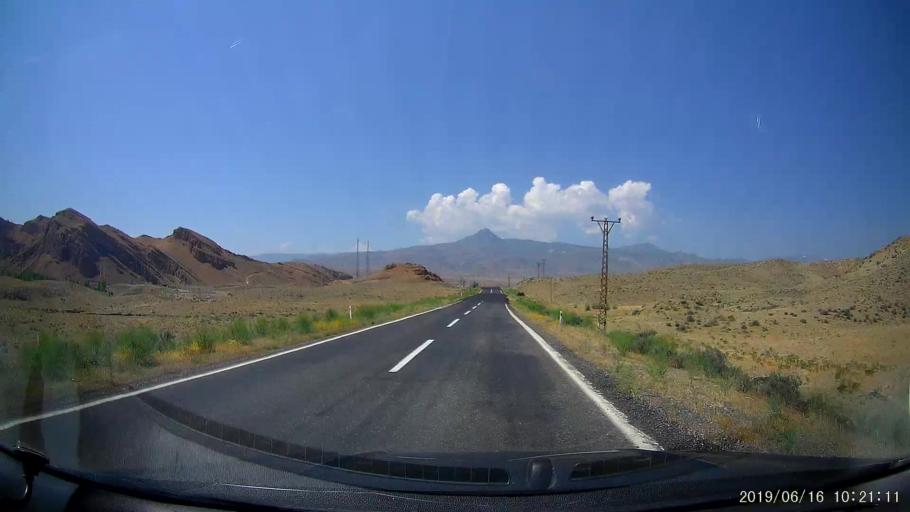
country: TR
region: Igdir
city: Tuzluca
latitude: 40.1404
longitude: 43.6398
